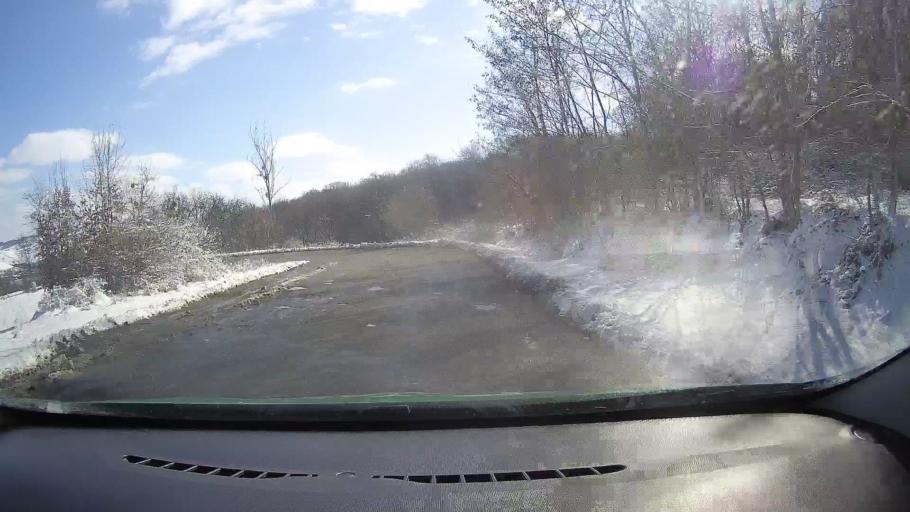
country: RO
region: Sibiu
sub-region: Comuna Altina
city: Altina
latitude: 45.9912
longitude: 24.4333
